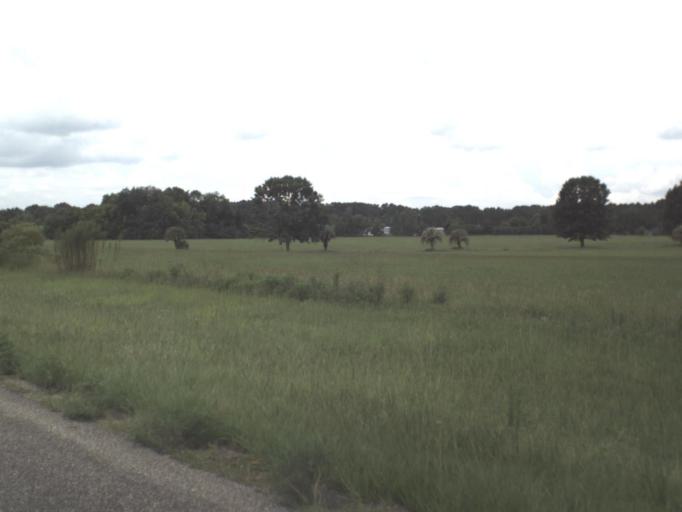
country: US
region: Florida
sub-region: Alachua County
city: Newberry
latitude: 29.6598
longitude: -82.6070
